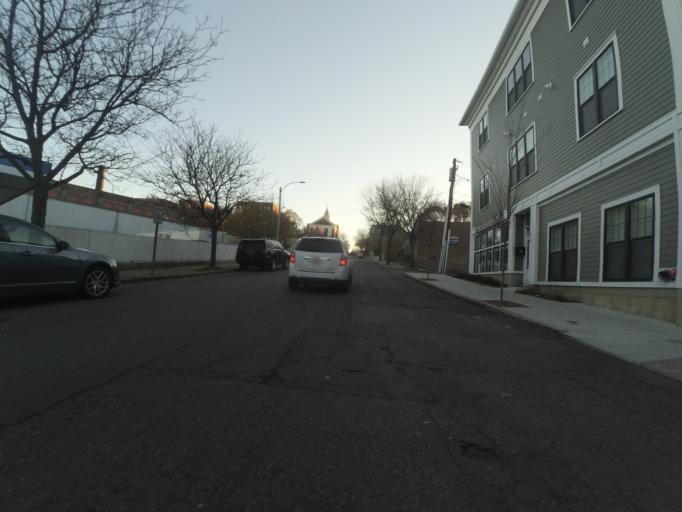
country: US
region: Massachusetts
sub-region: Middlesex County
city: Somerville
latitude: 42.3891
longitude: -71.0972
